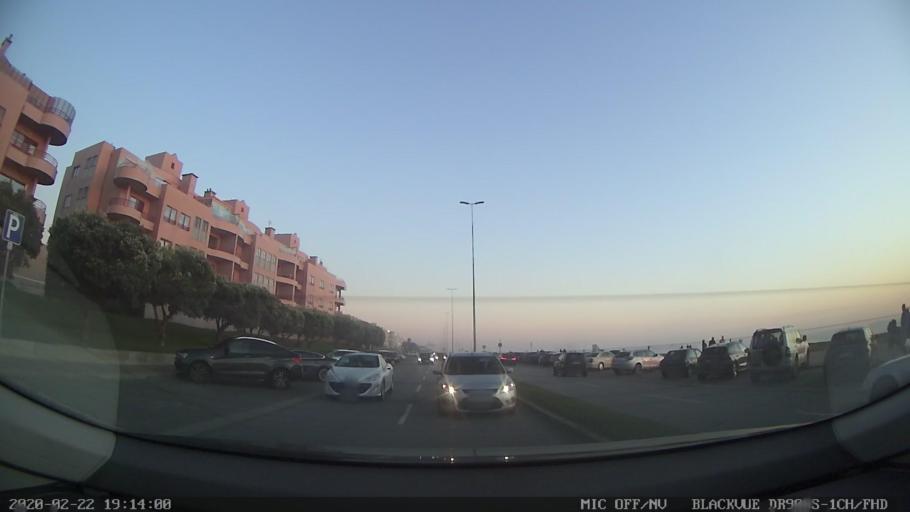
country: PT
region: Porto
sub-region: Matosinhos
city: Leca da Palmeira
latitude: 41.1967
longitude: -8.7092
